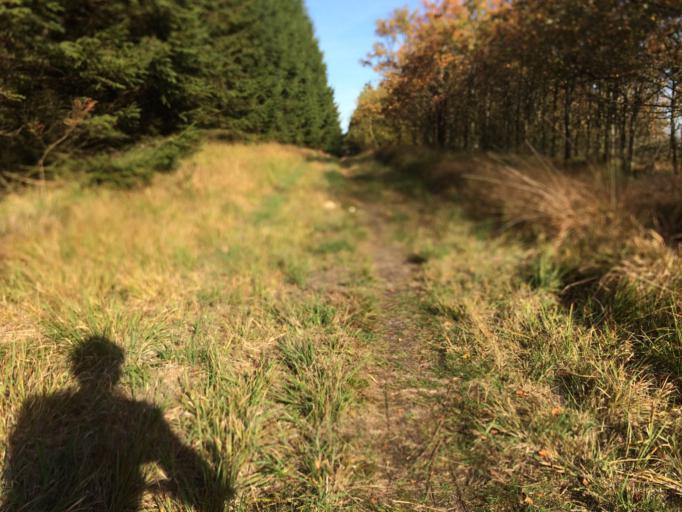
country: DK
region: Central Jutland
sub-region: Holstebro Kommune
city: Ulfborg
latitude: 56.2657
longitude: 8.4685
